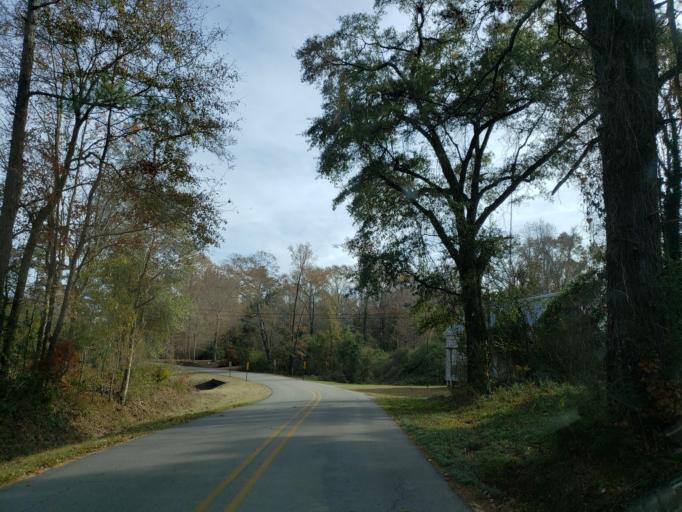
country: US
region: Mississippi
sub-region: Forrest County
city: Rawls Springs
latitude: 31.3789
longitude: -89.3705
